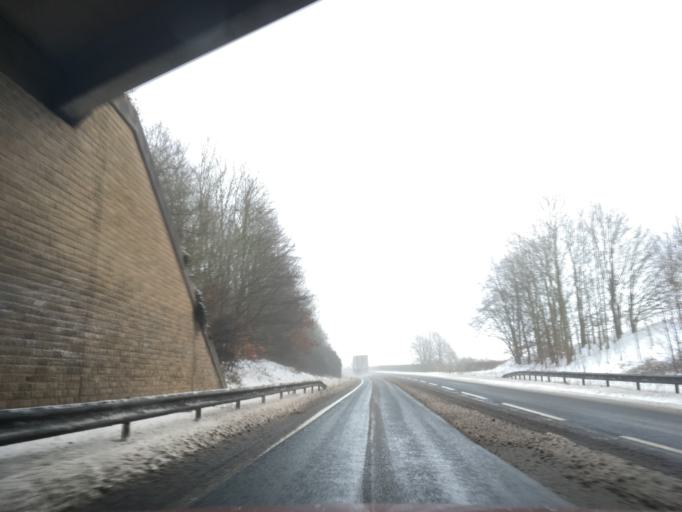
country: GB
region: England
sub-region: Warwickshire
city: Stratford-upon-Avon
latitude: 52.2319
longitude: -1.6870
